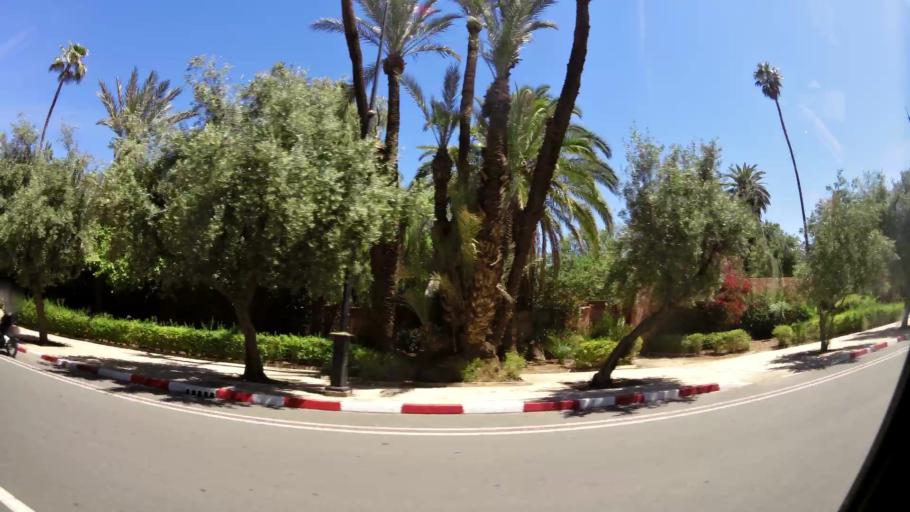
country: MA
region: Marrakech-Tensift-Al Haouz
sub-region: Marrakech
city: Marrakesh
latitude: 31.6277
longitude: -8.0109
